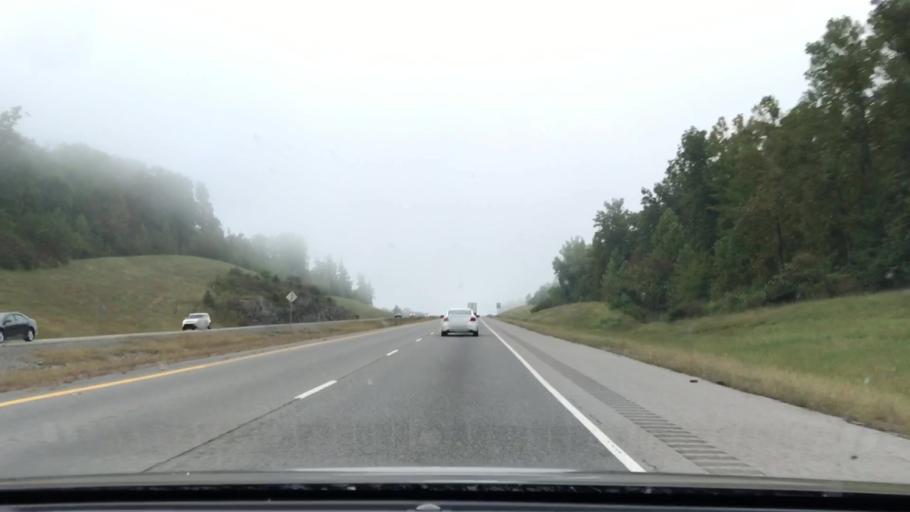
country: US
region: Tennessee
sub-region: Sumner County
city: Gallatin
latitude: 36.4726
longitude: -86.4736
